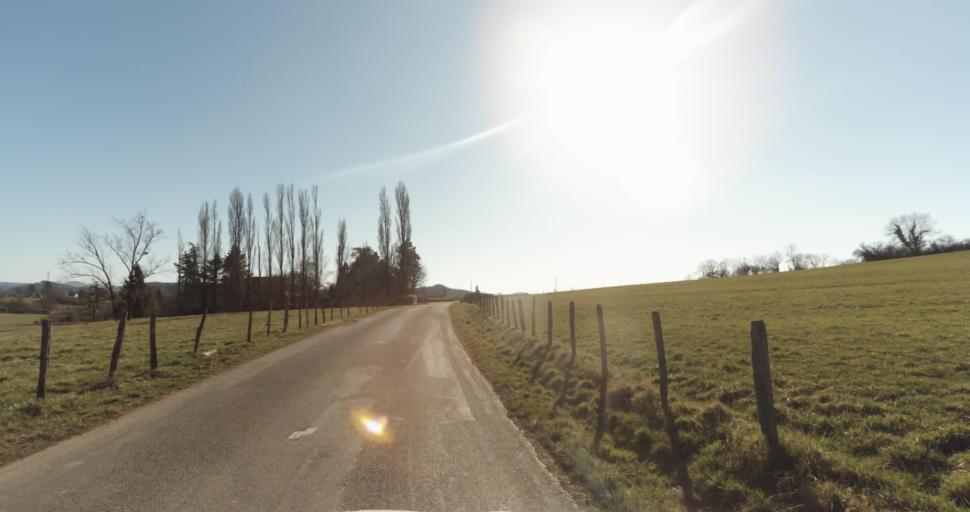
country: FR
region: Franche-Comte
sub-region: Departement du Jura
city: Montmorot
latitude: 46.6929
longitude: 5.5330
